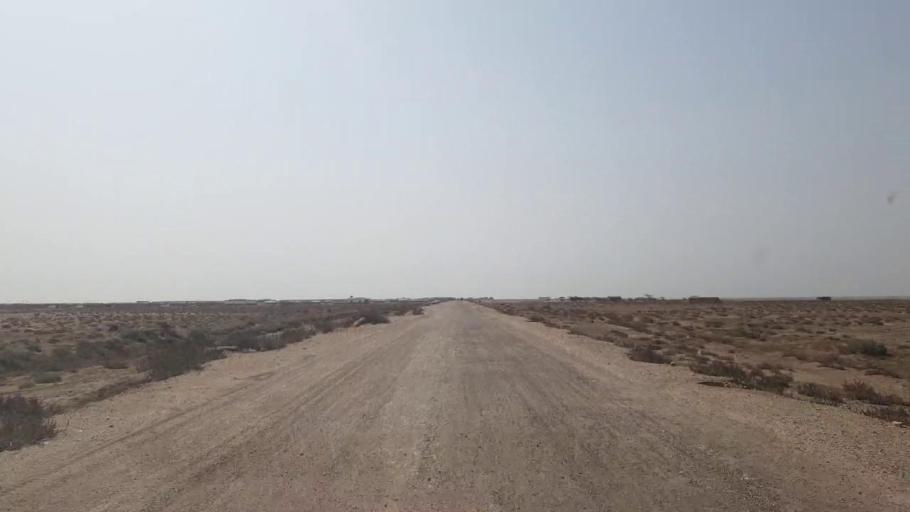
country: PK
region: Sindh
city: Jati
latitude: 24.3474
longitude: 68.5935
